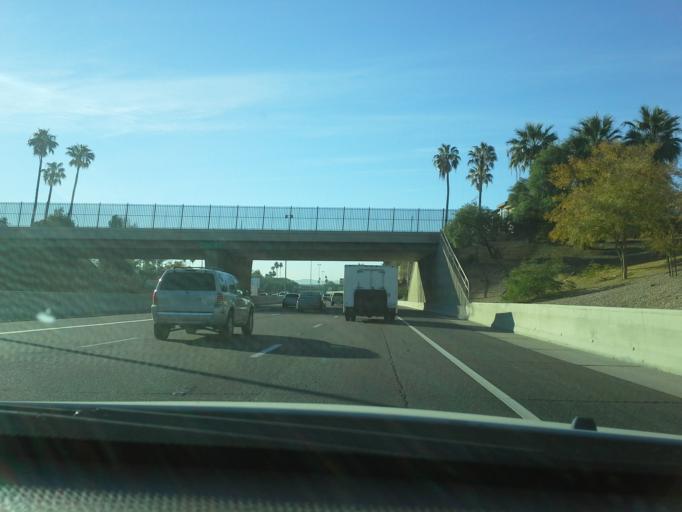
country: US
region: Arizona
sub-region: Maricopa County
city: Phoenix
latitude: 33.5136
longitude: -112.0444
